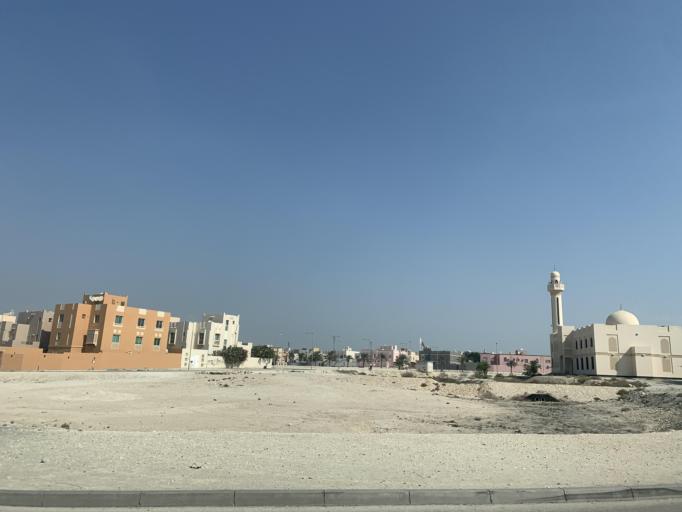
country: BH
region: Central Governorate
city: Madinat Hamad
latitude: 26.1084
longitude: 50.5018
